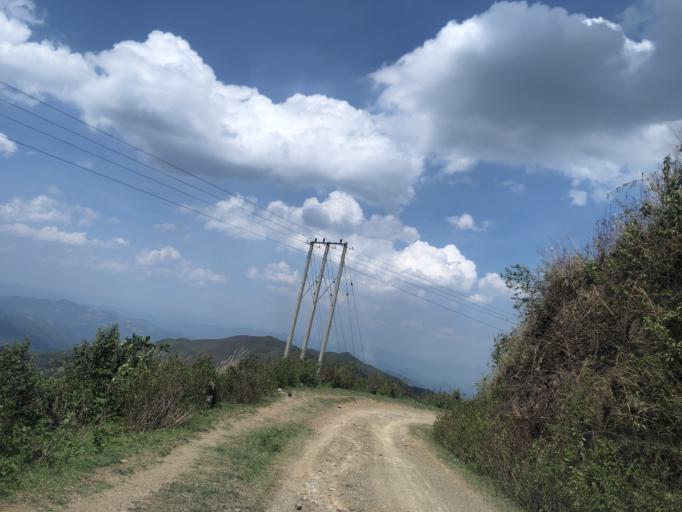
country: LA
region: Phongsali
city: Phongsali
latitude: 21.3973
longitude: 102.2154
